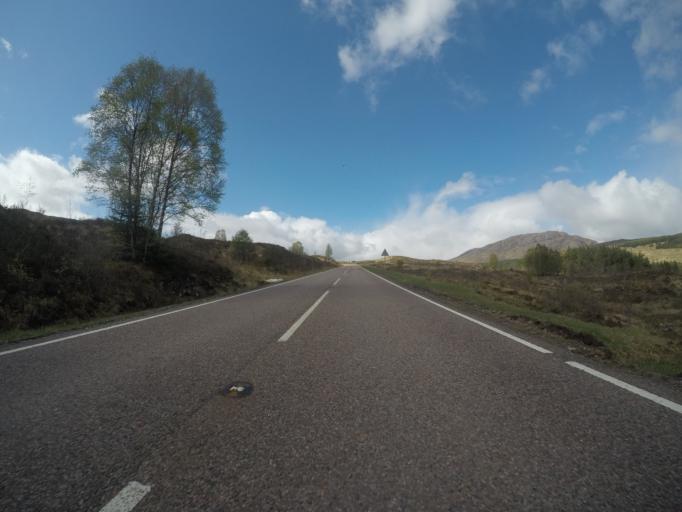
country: GB
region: Scotland
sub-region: Highland
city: Spean Bridge
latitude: 57.1256
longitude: -4.9674
